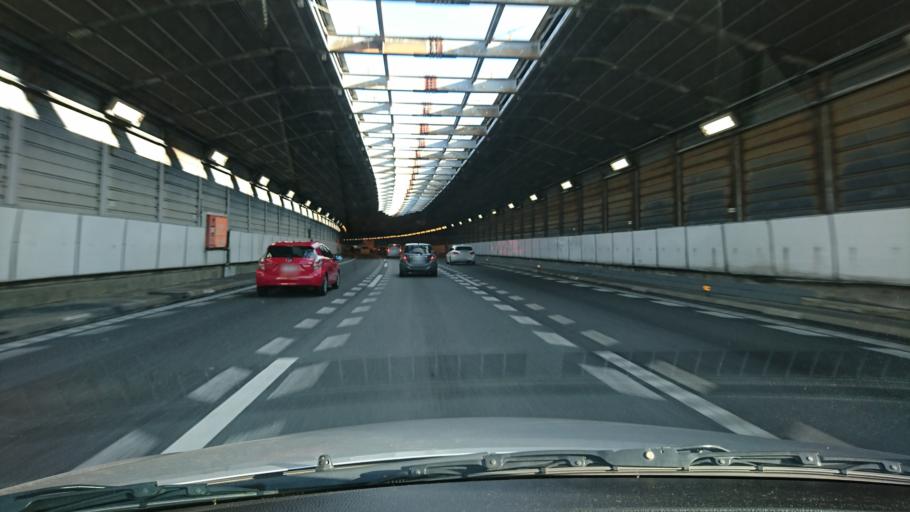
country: JP
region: Hyogo
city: Takarazuka
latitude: 34.8220
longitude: 135.3186
